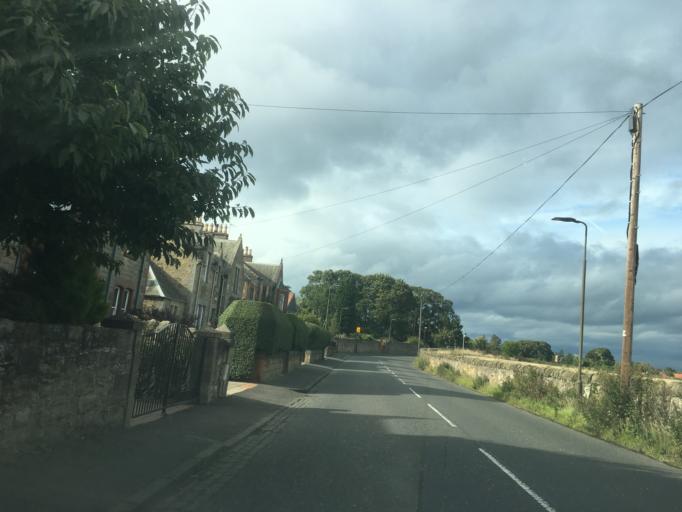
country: GB
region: Scotland
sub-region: East Lothian
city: Musselburgh
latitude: 55.9303
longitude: -3.0408
